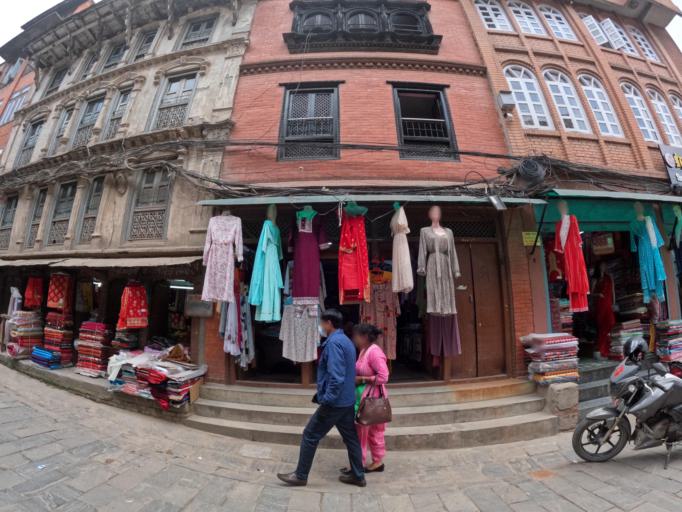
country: NP
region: Central Region
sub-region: Bagmati Zone
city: Bhaktapur
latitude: 27.6709
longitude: 85.4258
